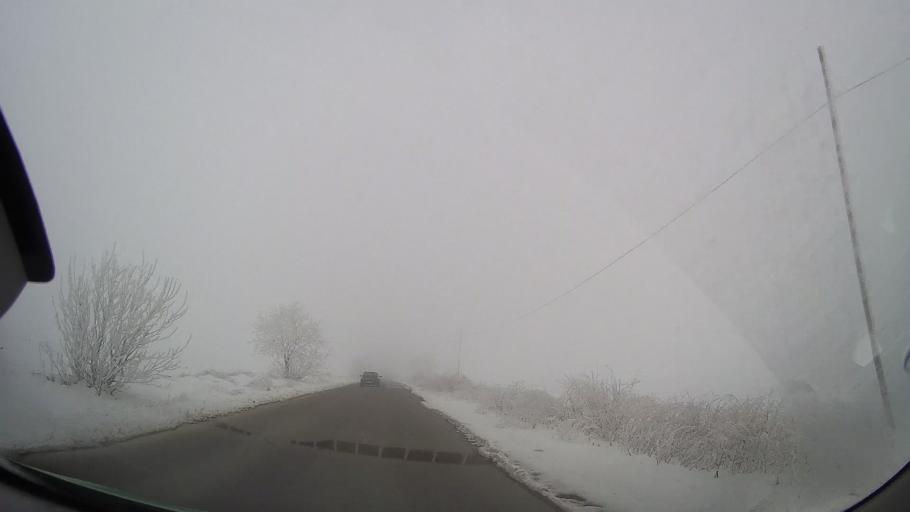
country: RO
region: Neamt
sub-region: Comuna Sabaoani
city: Sabaoani
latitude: 46.9928
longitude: 26.8629
